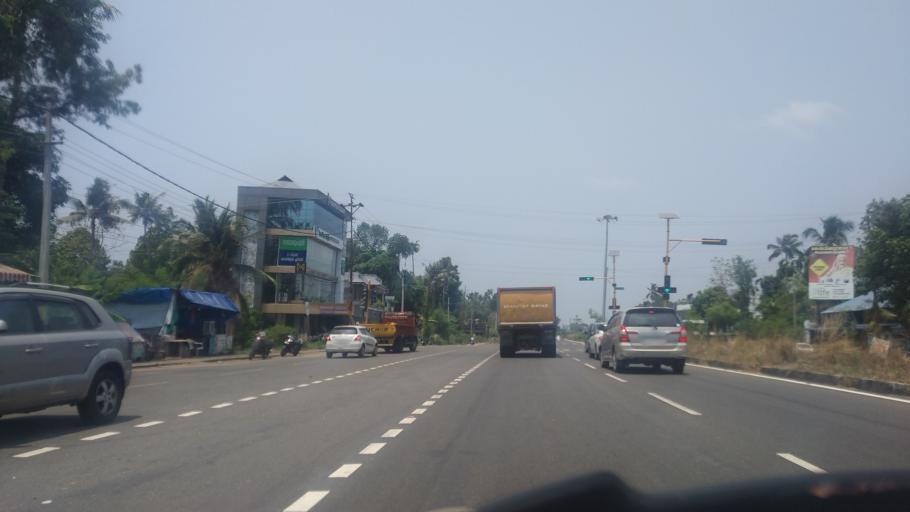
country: IN
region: Kerala
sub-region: Thrissur District
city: Kodungallur
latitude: 10.2202
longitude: 76.1959
